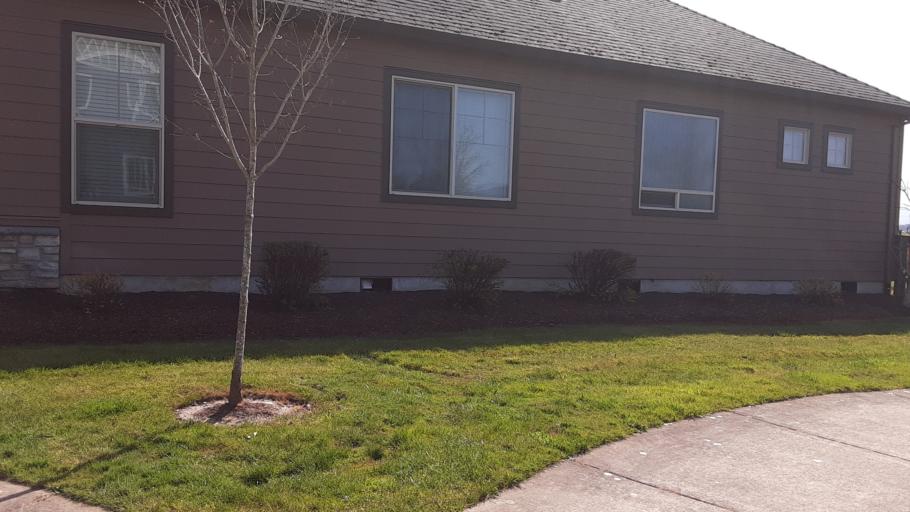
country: US
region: Oregon
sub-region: Benton County
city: Corvallis
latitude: 44.5291
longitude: -123.2613
